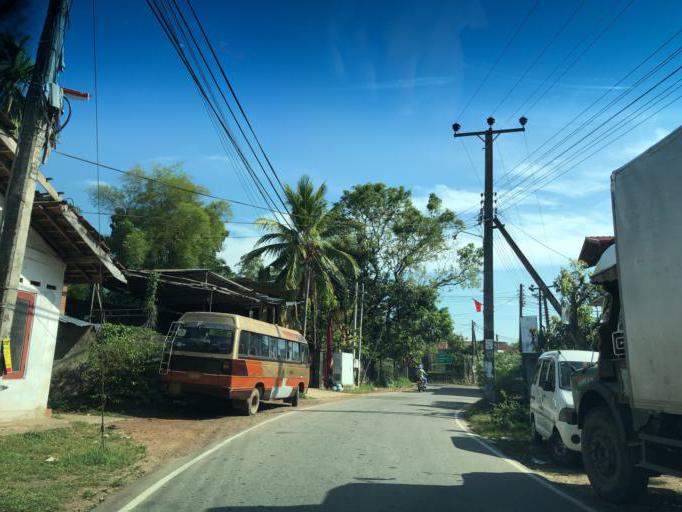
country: LK
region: Western
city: Homagama
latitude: 6.8064
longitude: 79.9790
